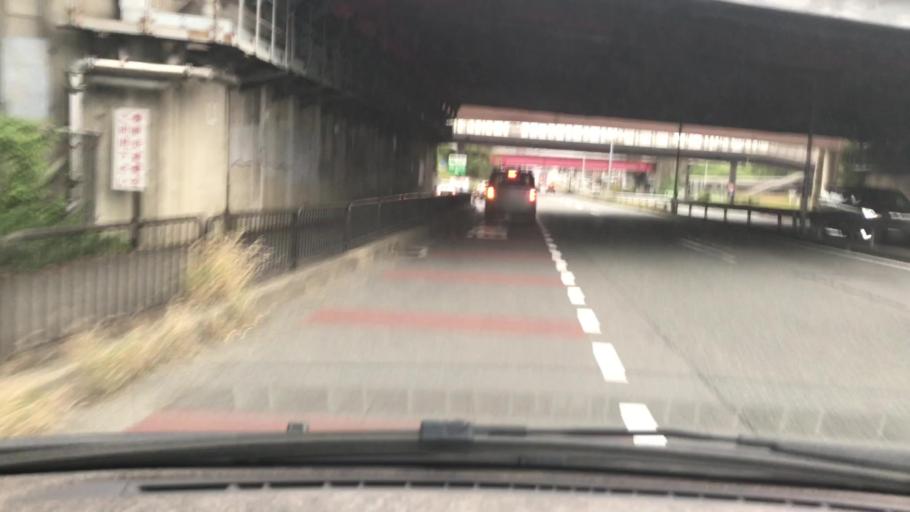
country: JP
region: Kyoto
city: Muko
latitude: 34.9542
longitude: 135.7456
